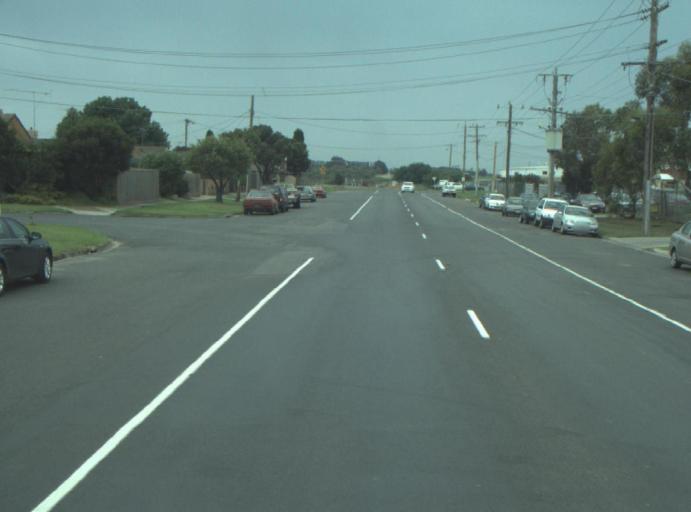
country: AU
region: Victoria
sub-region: Greater Geelong
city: Breakwater
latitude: -38.1845
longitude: 144.3816
